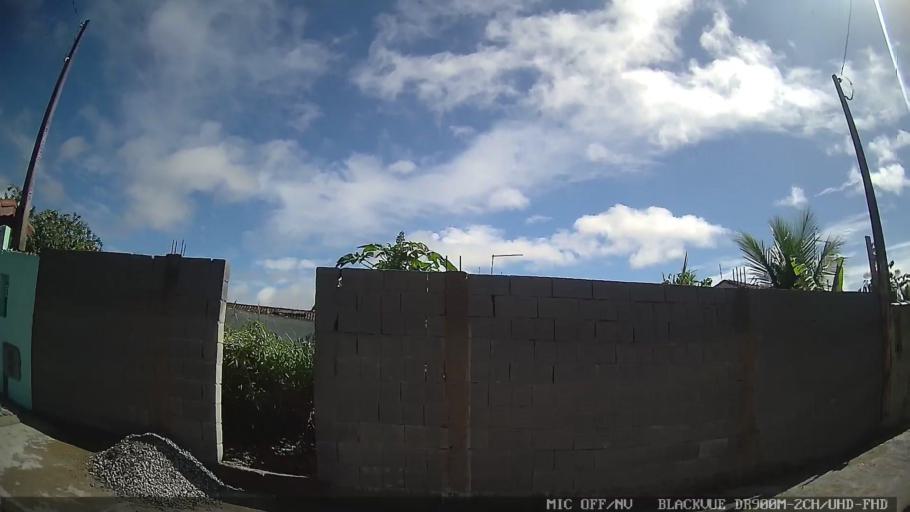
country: BR
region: Sao Paulo
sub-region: Itanhaem
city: Itanhaem
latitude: -24.2389
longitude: -46.8834
